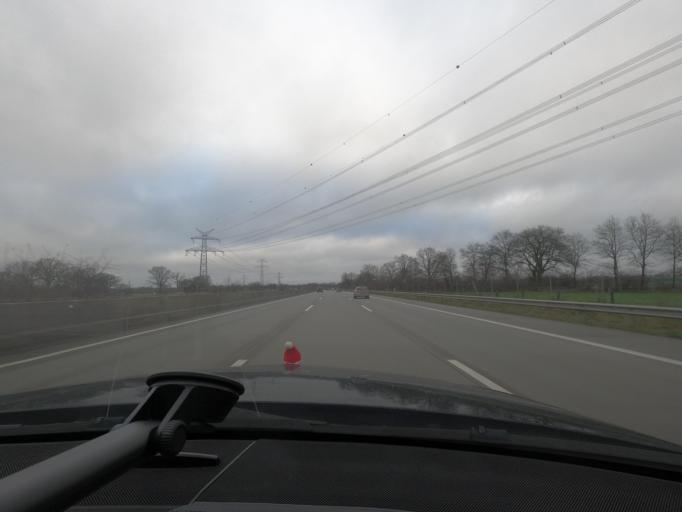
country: DE
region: Schleswig-Holstein
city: Nutzen
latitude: 53.8626
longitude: 9.9451
